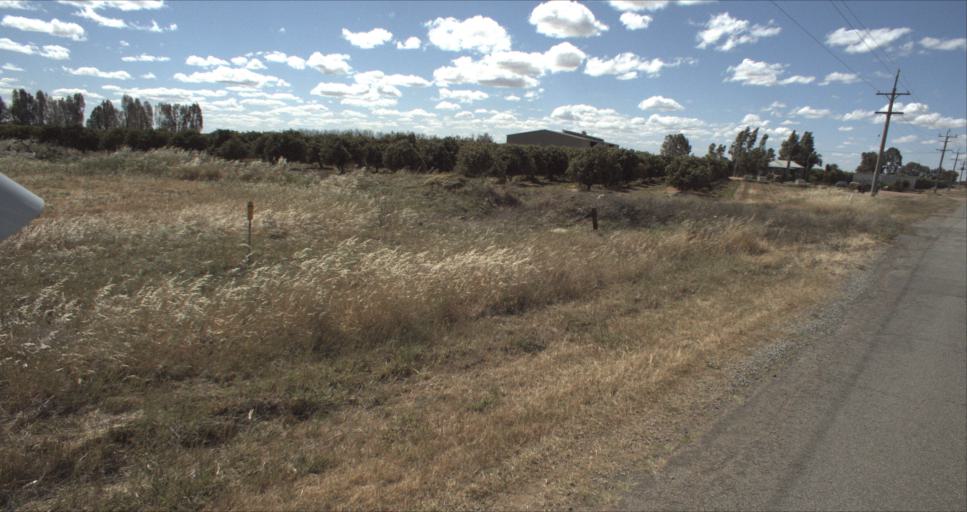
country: AU
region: New South Wales
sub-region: Leeton
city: Leeton
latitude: -34.5120
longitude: 146.2526
